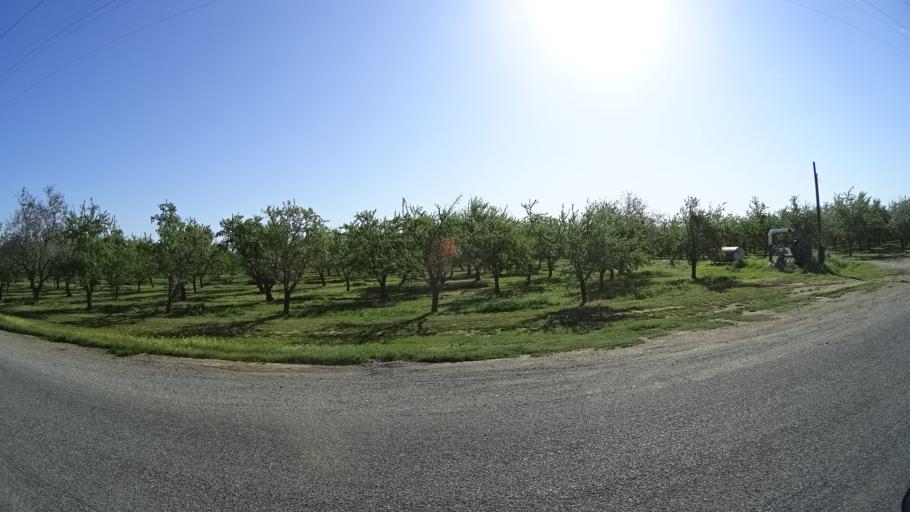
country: US
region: California
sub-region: Glenn County
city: Hamilton City
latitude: 39.7708
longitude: -122.0854
